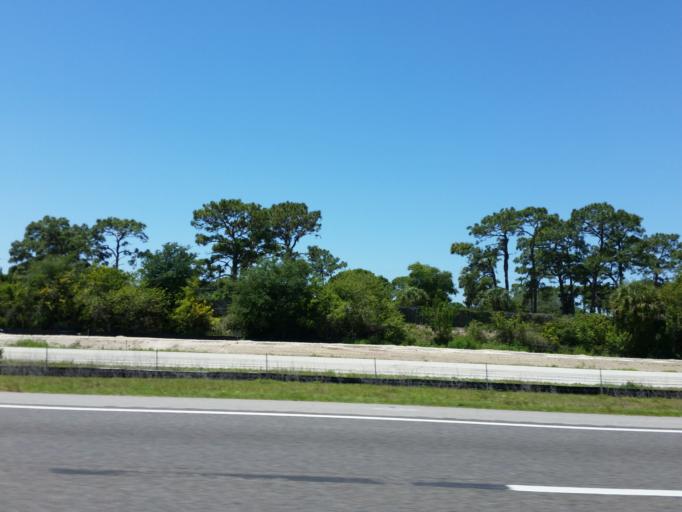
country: US
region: Florida
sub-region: Sarasota County
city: Nokomis
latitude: 27.1464
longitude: -82.4172
